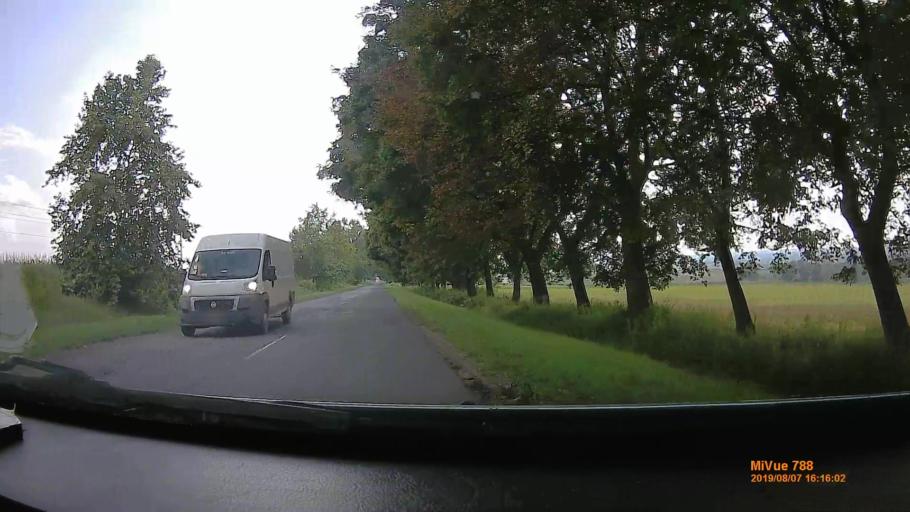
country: HU
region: Borsod-Abauj-Zemplen
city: Gonc
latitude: 48.4652
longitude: 21.2516
